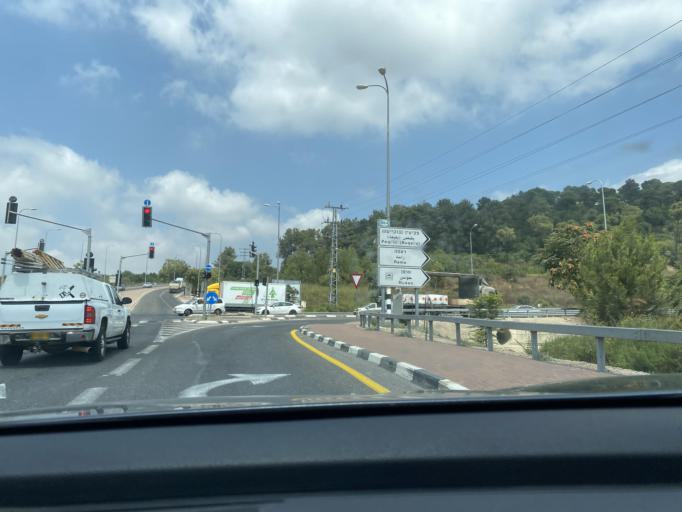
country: IL
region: Northern District
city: Kefar Weradim
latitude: 33.0046
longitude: 35.2953
